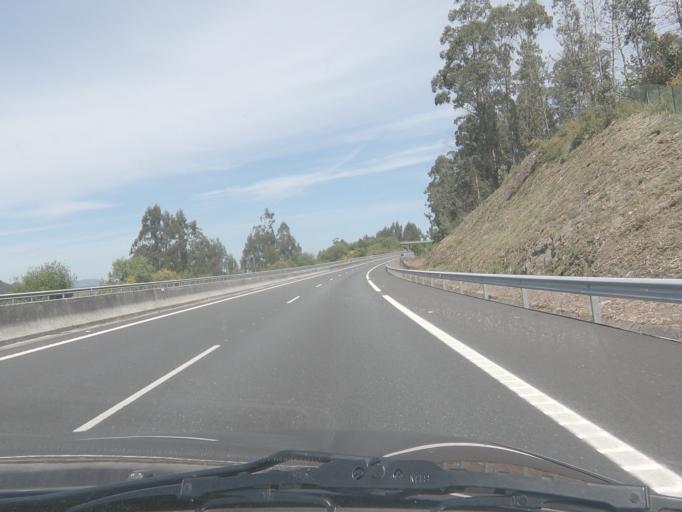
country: ES
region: Galicia
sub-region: Provincia de Pontevedra
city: Valga
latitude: 42.6509
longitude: -8.6514
